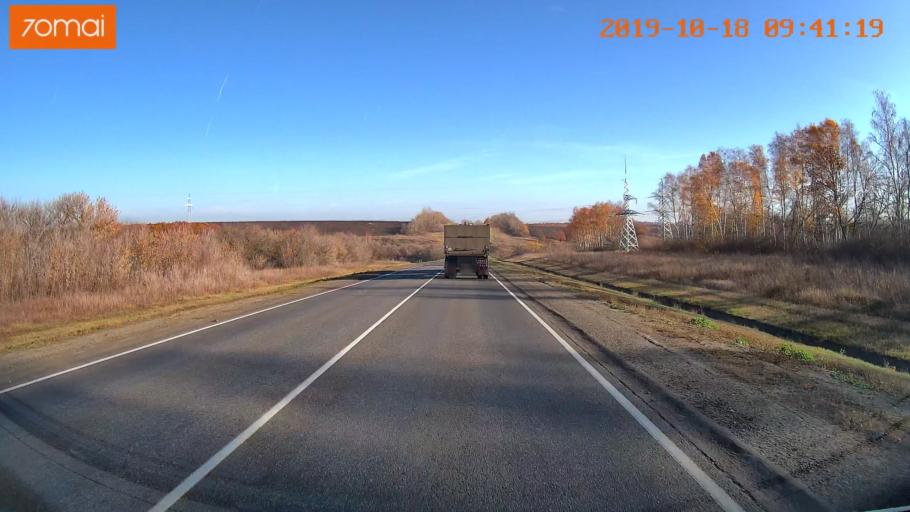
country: RU
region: Tula
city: Kazachka
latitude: 53.2736
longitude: 38.1602
